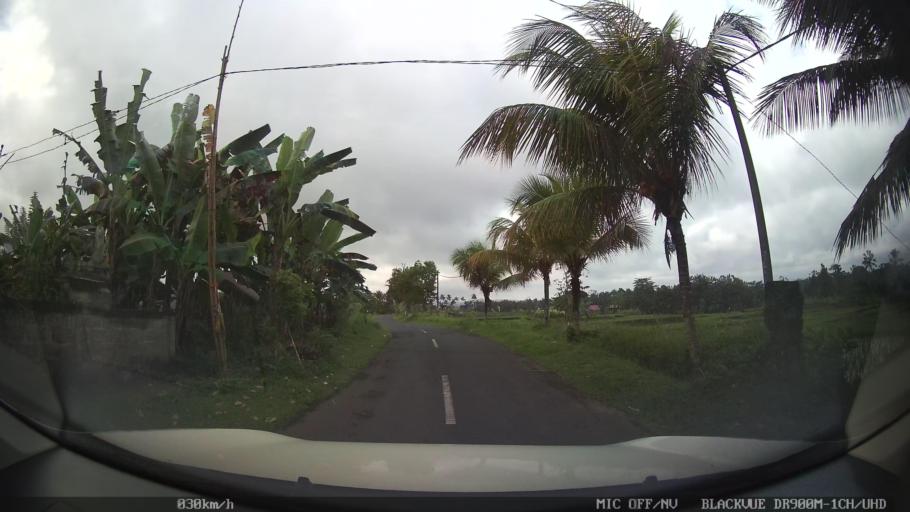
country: ID
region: Bali
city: Badung
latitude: -8.4221
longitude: 115.2272
